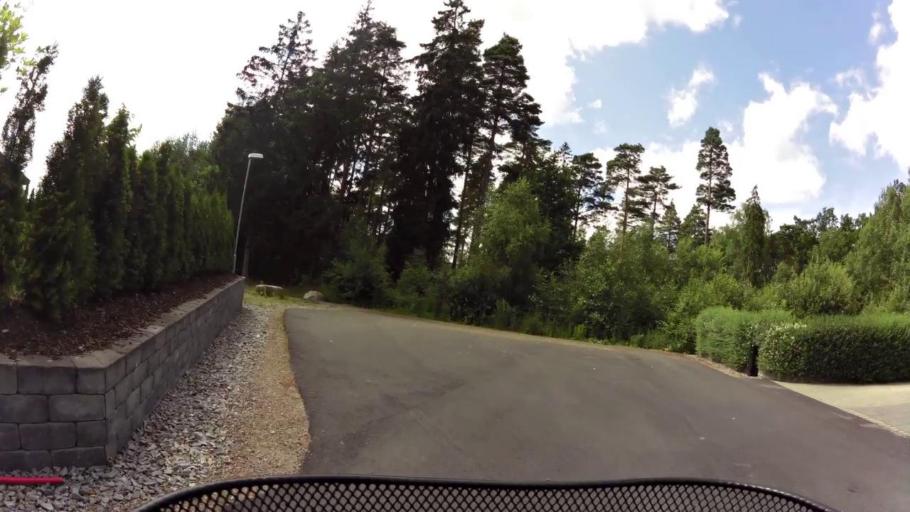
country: SE
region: OEstergoetland
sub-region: Linkopings Kommun
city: Ekangen
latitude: 58.4794
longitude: 15.6342
